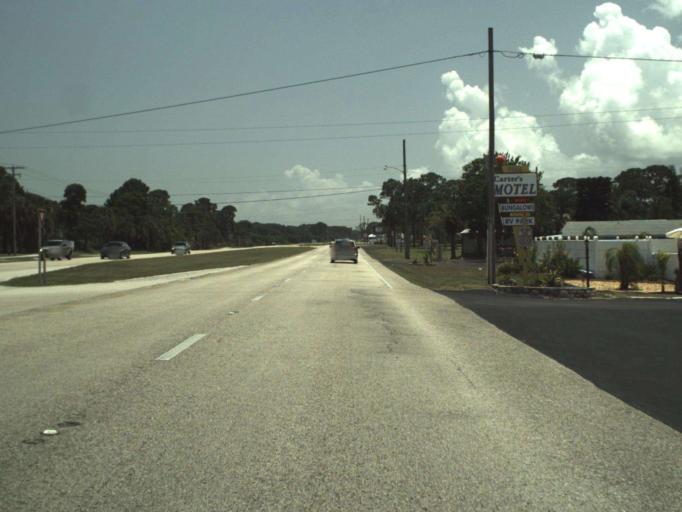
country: US
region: Florida
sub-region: Volusia County
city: Edgewater
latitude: 28.9592
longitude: -80.8883
